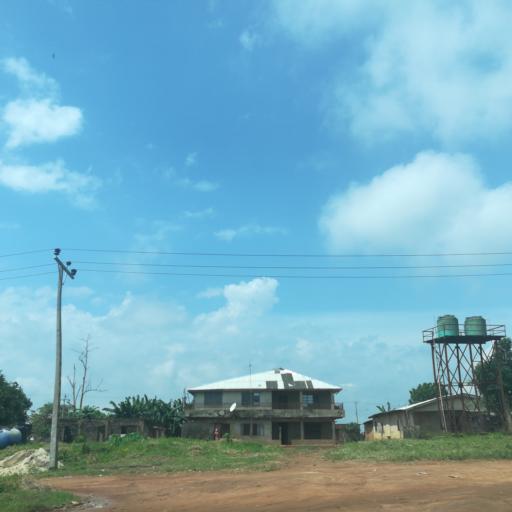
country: NG
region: Lagos
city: Ikorodu
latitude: 6.6627
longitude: 3.6779
